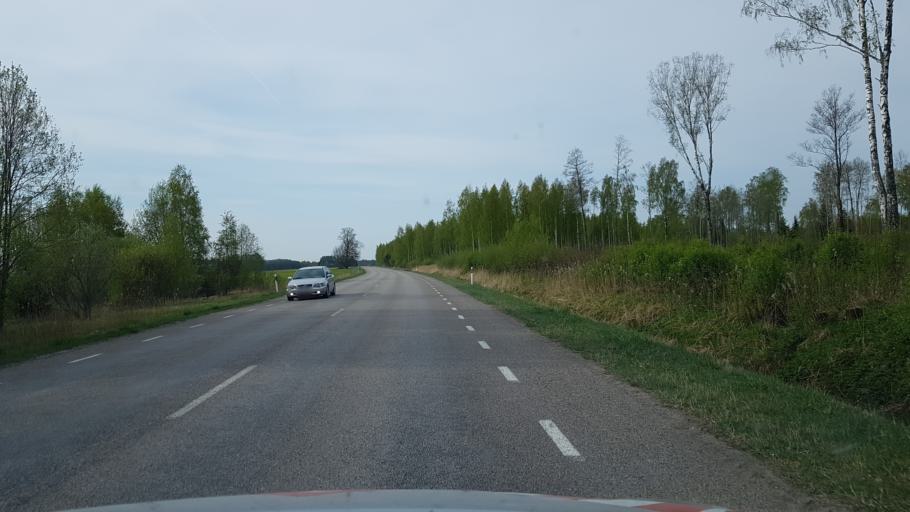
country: EE
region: Paernumaa
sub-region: Audru vald
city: Audru
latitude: 58.3866
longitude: 24.2733
